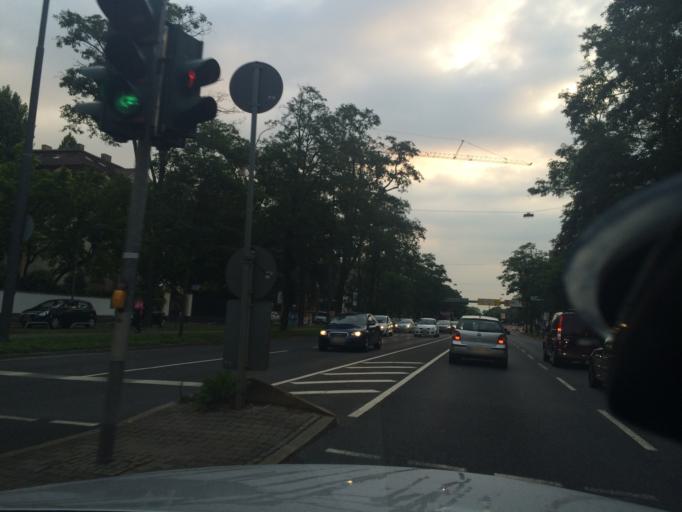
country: DE
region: Hesse
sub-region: Regierungsbezirk Darmstadt
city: Frankfurt am Main
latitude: 50.0953
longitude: 8.6681
